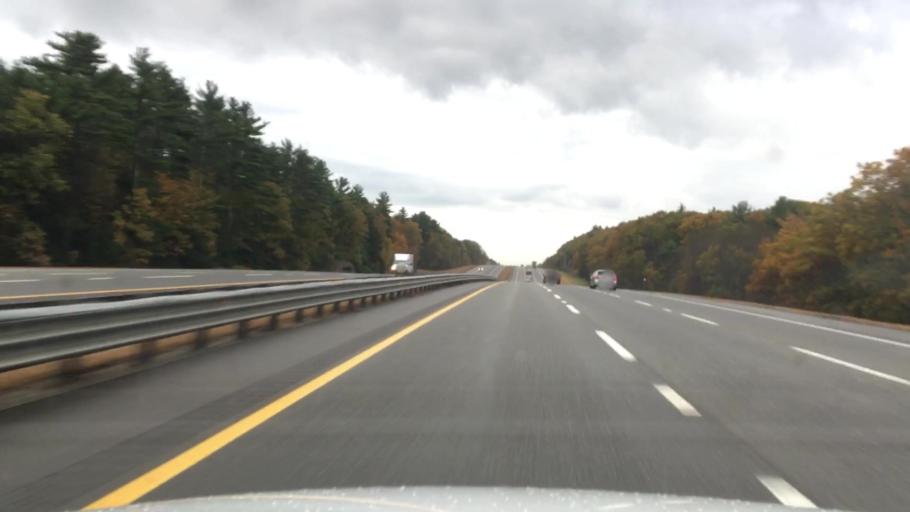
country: US
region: Maine
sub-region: York County
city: Cape Neddick
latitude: 43.2201
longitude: -70.6383
